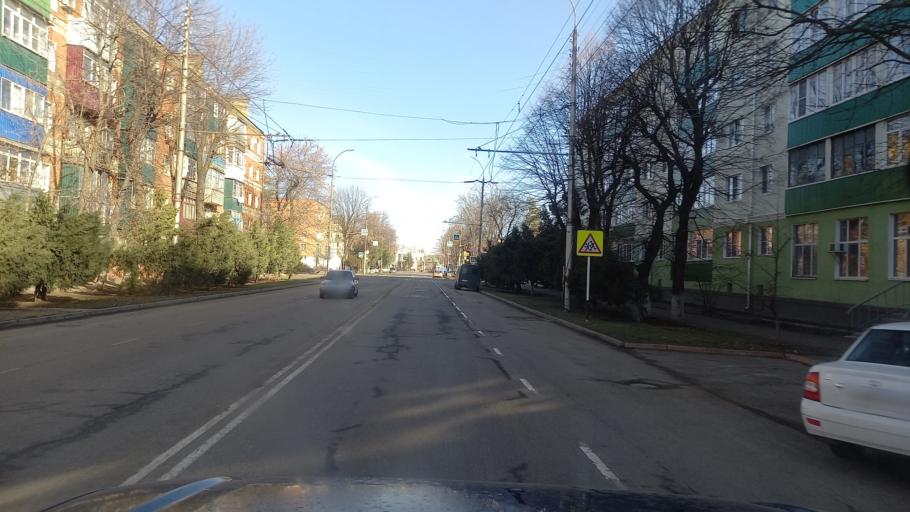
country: RU
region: Adygeya
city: Maykop
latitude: 44.6162
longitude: 40.1090
